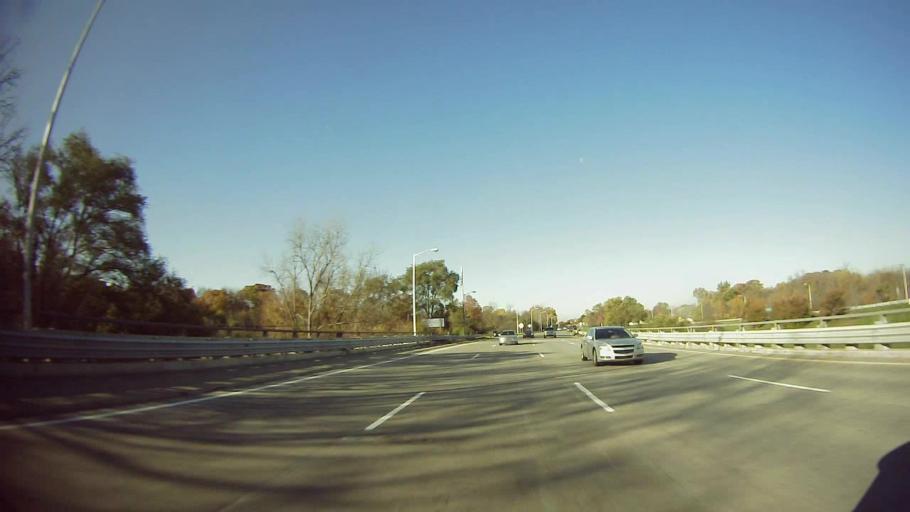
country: US
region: Michigan
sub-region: Wayne County
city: Dearborn Heights
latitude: 42.3269
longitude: -83.2456
